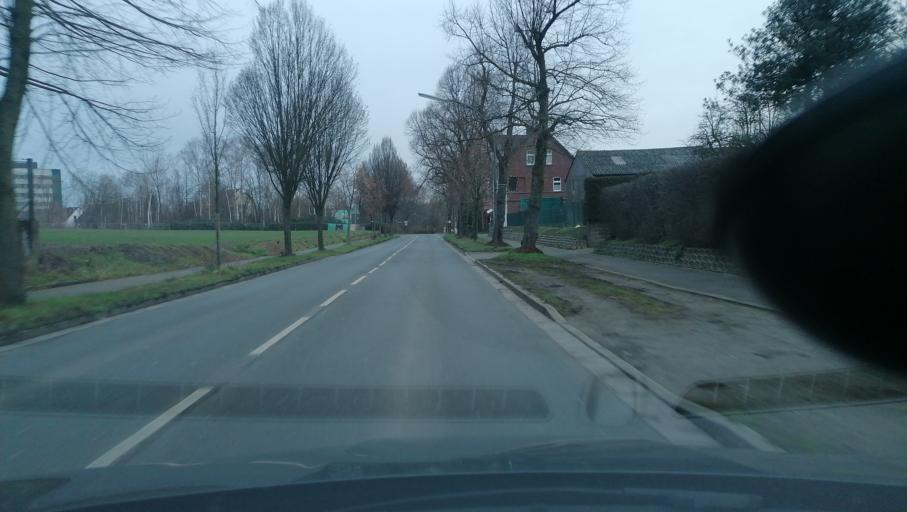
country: DE
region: North Rhine-Westphalia
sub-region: Regierungsbezirk Munster
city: Recklinghausen
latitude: 51.6036
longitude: 7.2321
